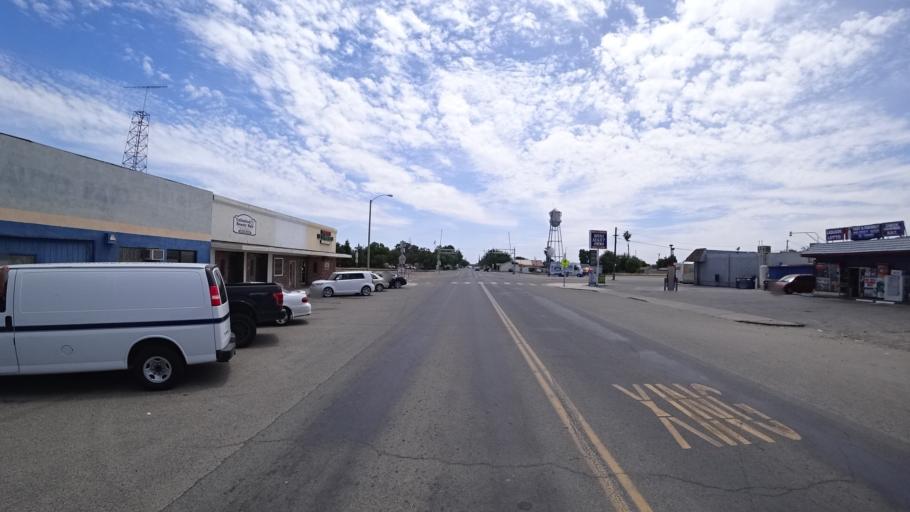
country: US
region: California
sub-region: Kings County
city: Armona
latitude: 36.3162
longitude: -119.7090
